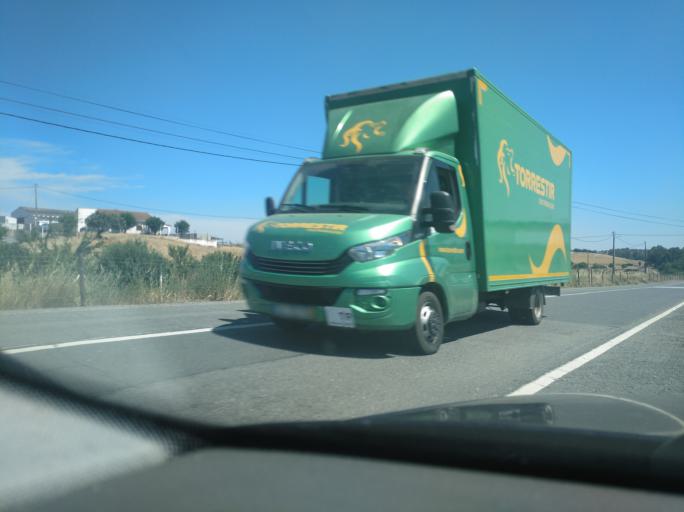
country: PT
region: Beja
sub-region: Castro Verde
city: Castro Verde
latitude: 37.6872
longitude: -8.0840
